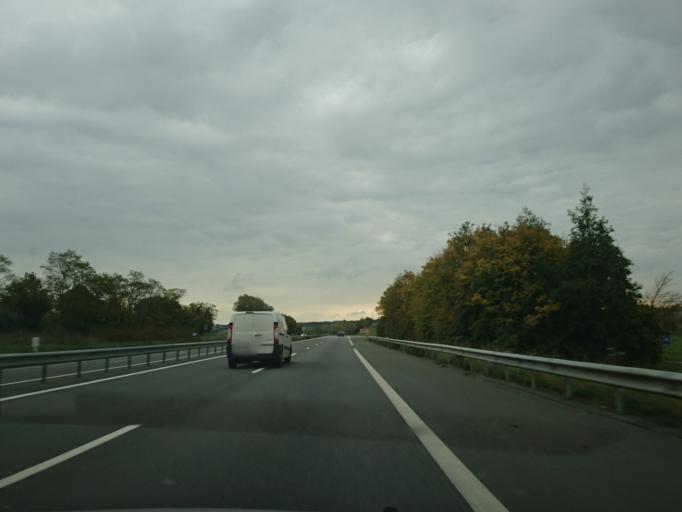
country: FR
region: Brittany
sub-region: Departement des Cotes-d'Armor
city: Broons
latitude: 48.3074
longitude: -2.2369
